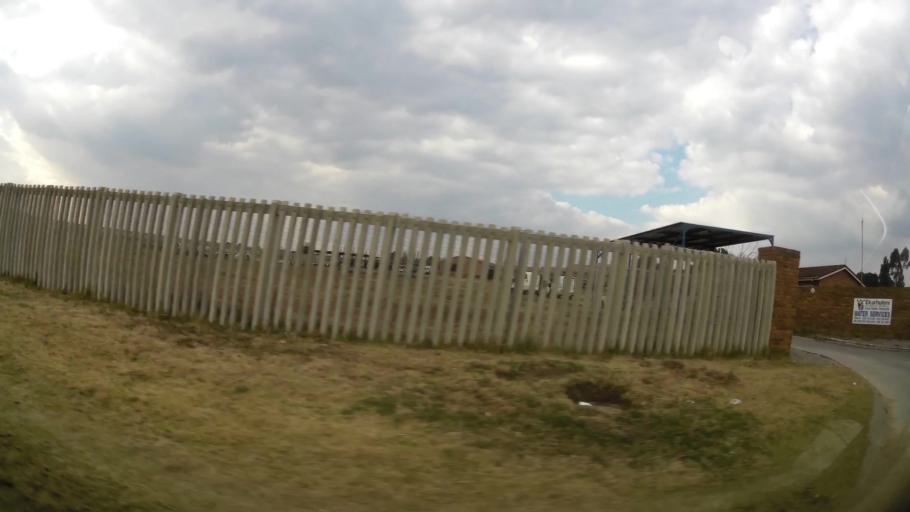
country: ZA
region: Gauteng
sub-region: Ekurhuleni Metropolitan Municipality
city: Benoni
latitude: -26.1404
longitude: 28.3547
